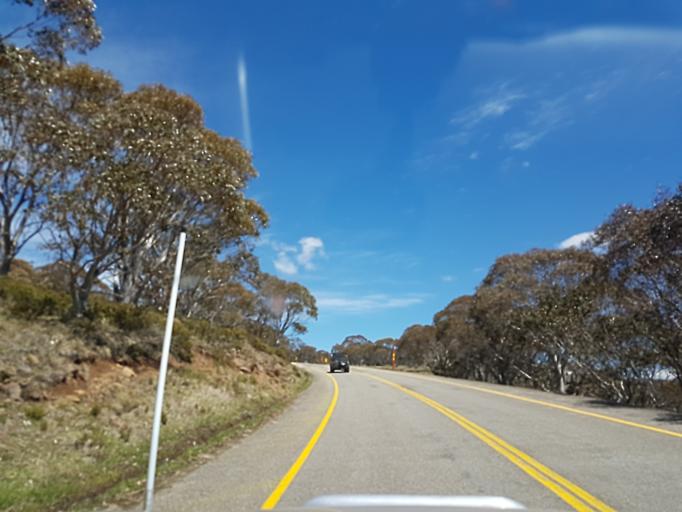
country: AU
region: Victoria
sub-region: Alpine
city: Mount Beauty
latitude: -37.0202
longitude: 147.2583
